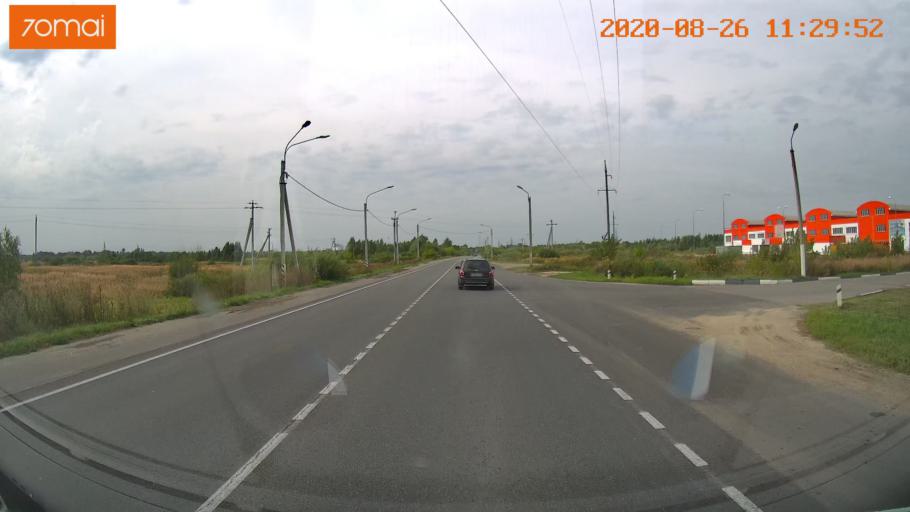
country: RU
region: Rjazan
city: Shilovo
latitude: 54.3179
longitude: 40.8932
